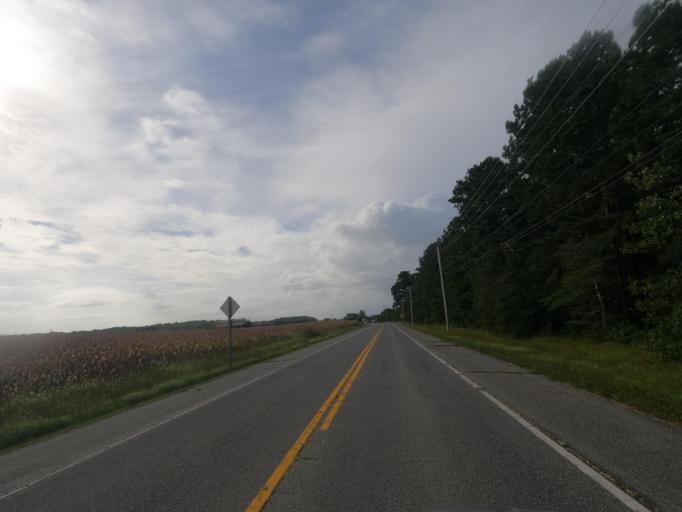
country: US
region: Virginia
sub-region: Northumberland County
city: Heathsville
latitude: 38.0839
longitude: -76.3582
